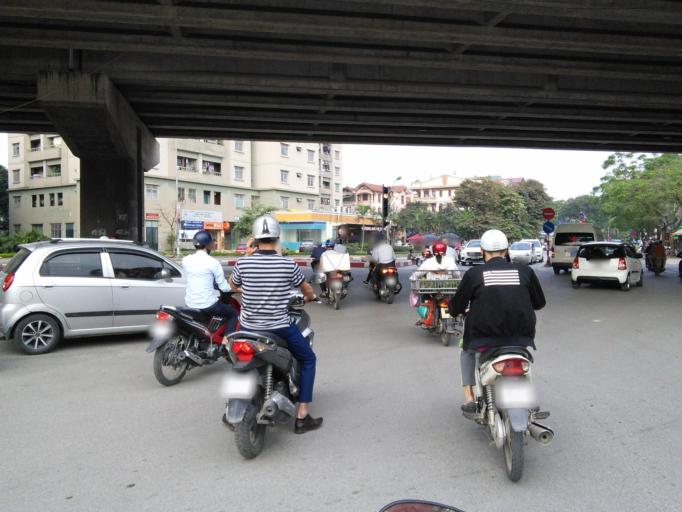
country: VN
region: Ha Noi
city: Van Dien
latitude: 20.9689
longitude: 105.8286
